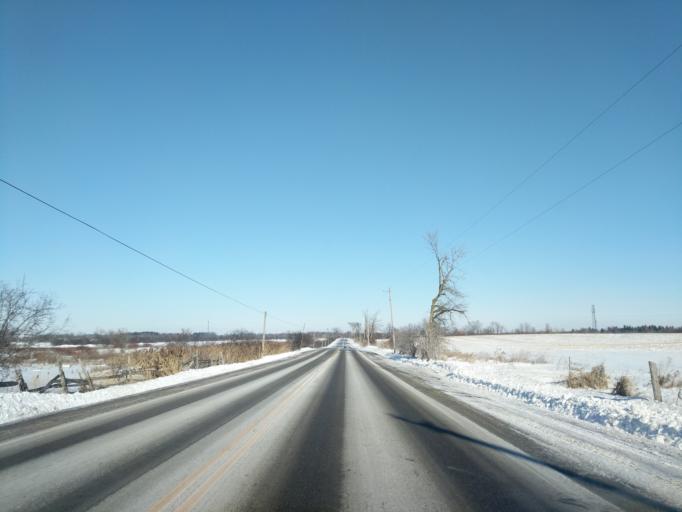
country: CA
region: Ontario
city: Pickering
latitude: 43.8574
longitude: -79.1319
